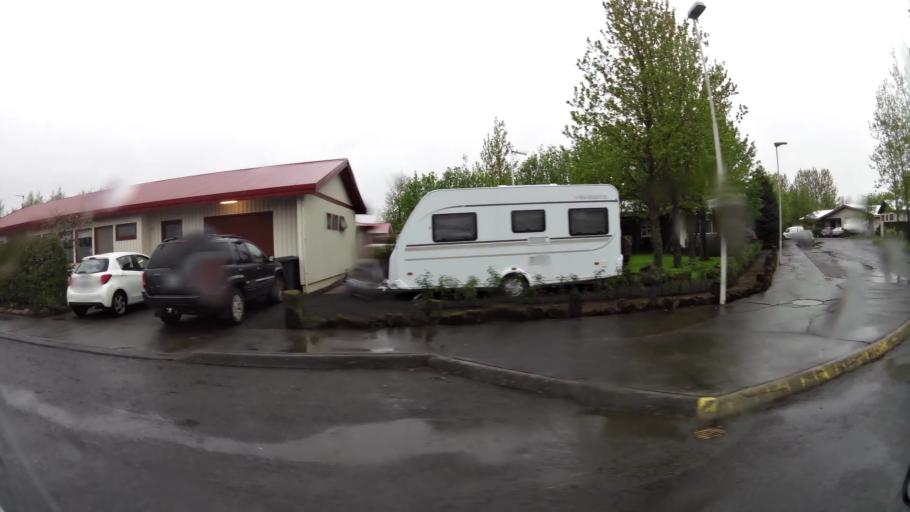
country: IS
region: South
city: Selfoss
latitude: 63.9287
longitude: -20.9940
